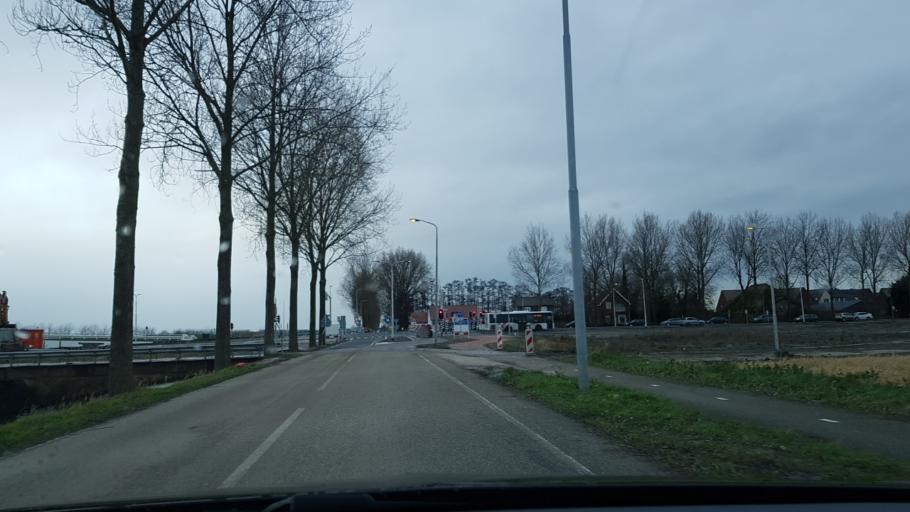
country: NL
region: North Holland
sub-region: Gemeente Haarlemmermeer
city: Hoofddorp
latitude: 52.2842
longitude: 4.6653
